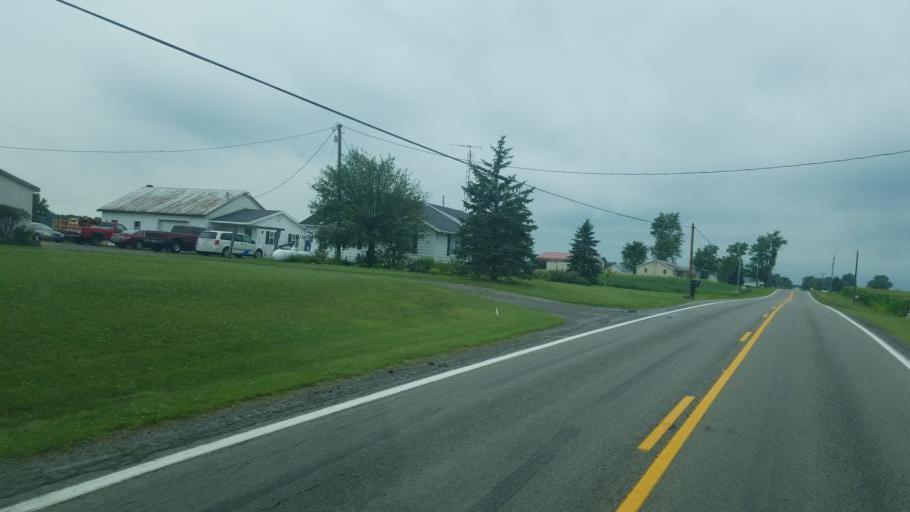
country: US
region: Ohio
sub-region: Logan County
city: Northwood
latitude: 40.5963
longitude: -83.7528
